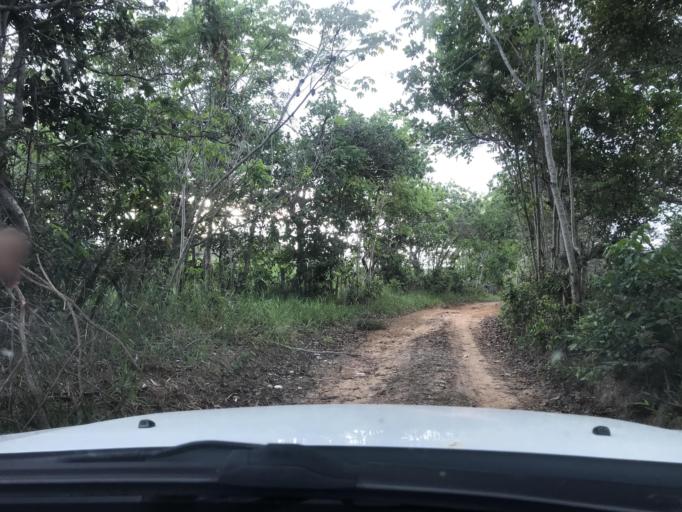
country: BR
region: Bahia
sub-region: Entre Rios
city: Entre Rios
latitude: -12.0521
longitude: -38.2154
